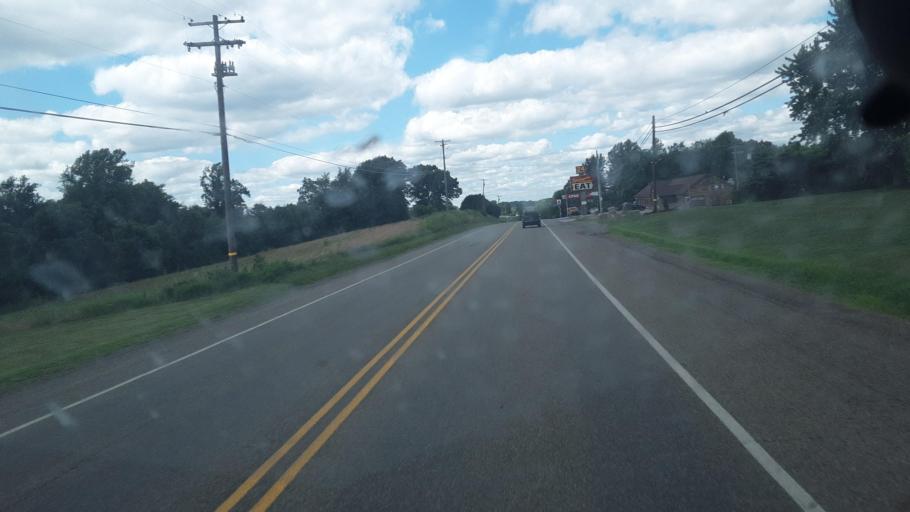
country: US
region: Pennsylvania
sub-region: Butler County
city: Prospect
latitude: 40.9488
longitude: -80.1538
